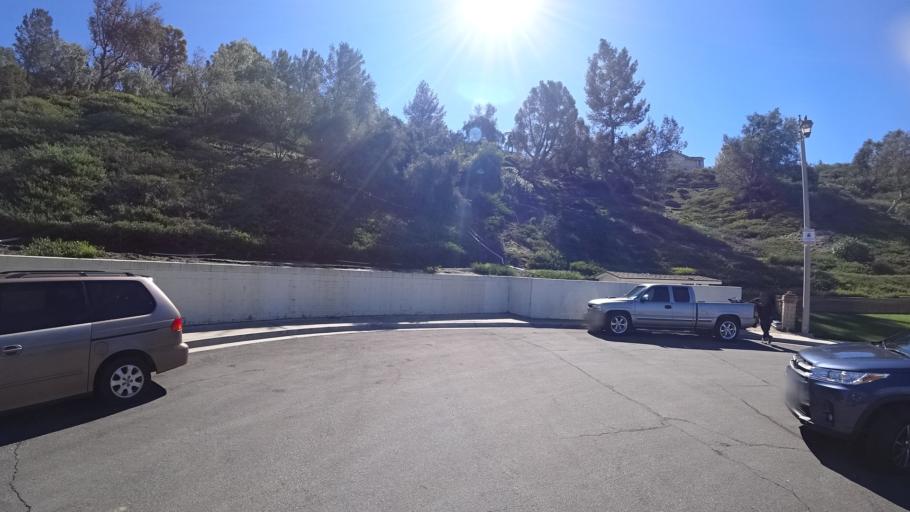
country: US
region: California
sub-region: Orange County
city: Yorba Linda
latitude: 33.8604
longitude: -117.7491
